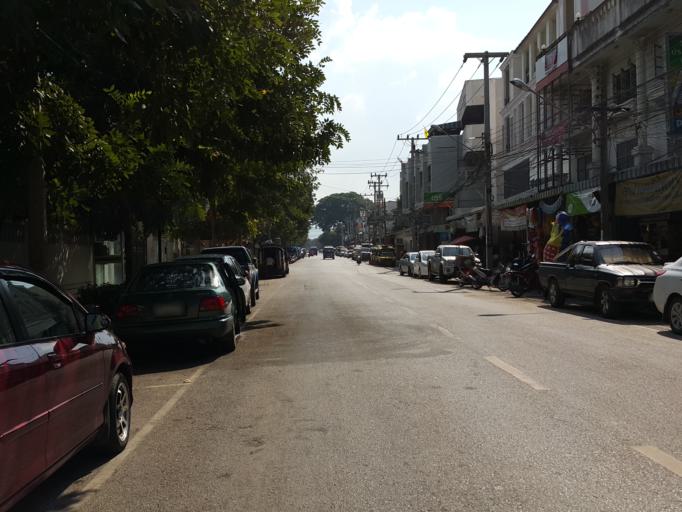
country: TH
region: Lampang
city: Lampang
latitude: 18.2871
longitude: 99.5045
